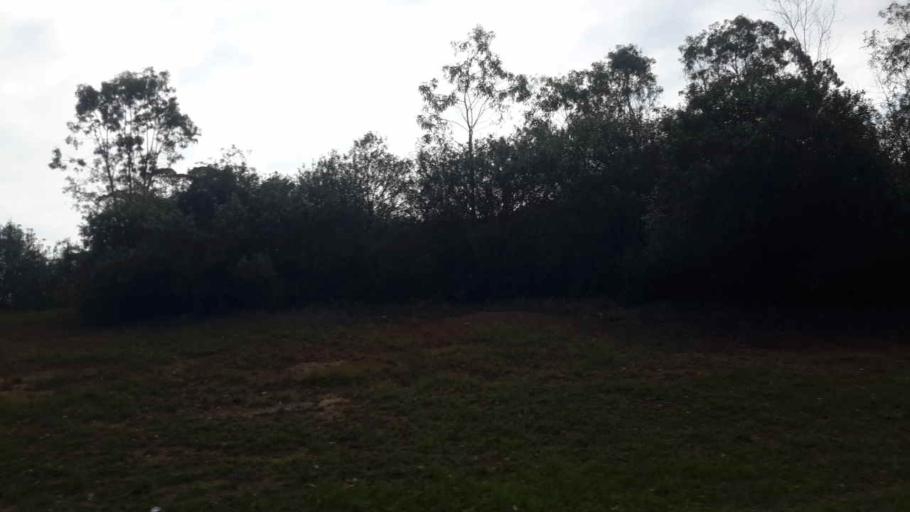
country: AU
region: New South Wales
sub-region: Campbelltown Municipality
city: Glen Alpine
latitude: -34.0886
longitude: 150.7739
